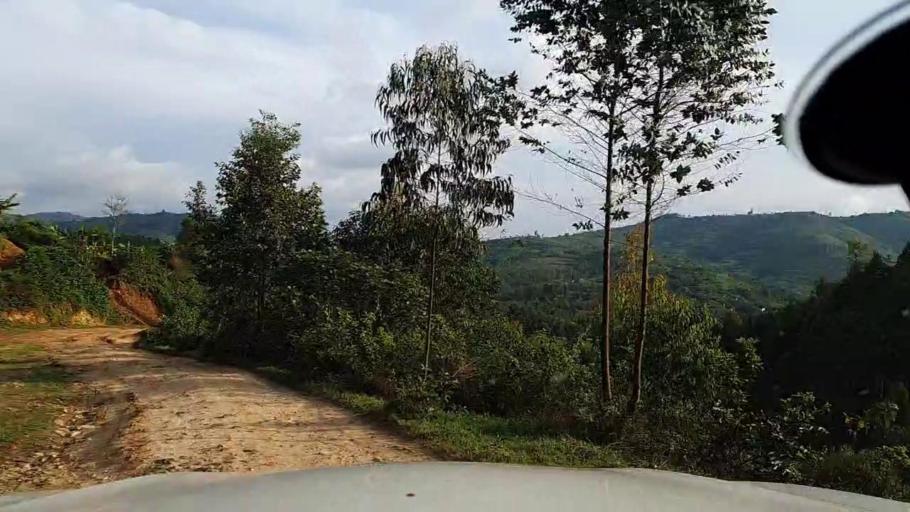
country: RW
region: Southern Province
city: Gitarama
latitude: -2.1919
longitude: 29.5784
